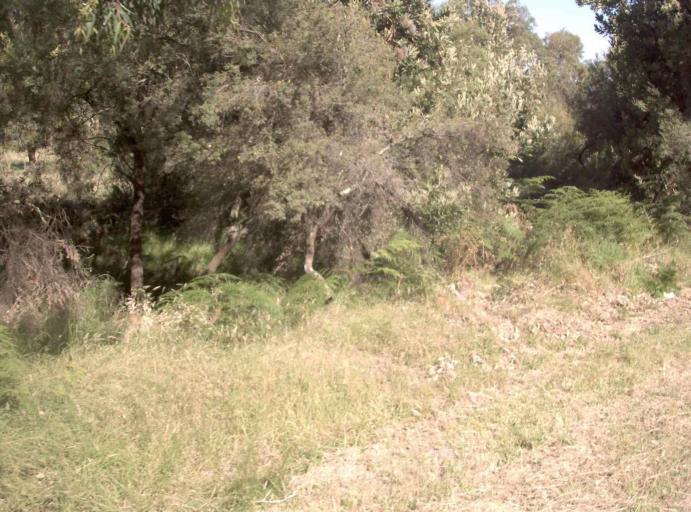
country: AU
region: Victoria
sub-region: Latrobe
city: Traralgon
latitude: -38.6464
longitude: 146.6729
